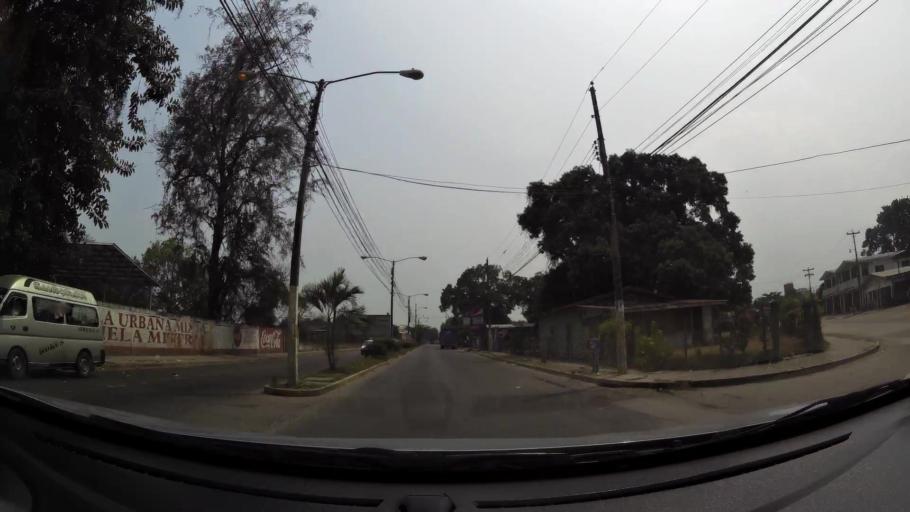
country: HN
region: Cortes
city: La Lima
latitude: 15.4395
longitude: -87.9301
